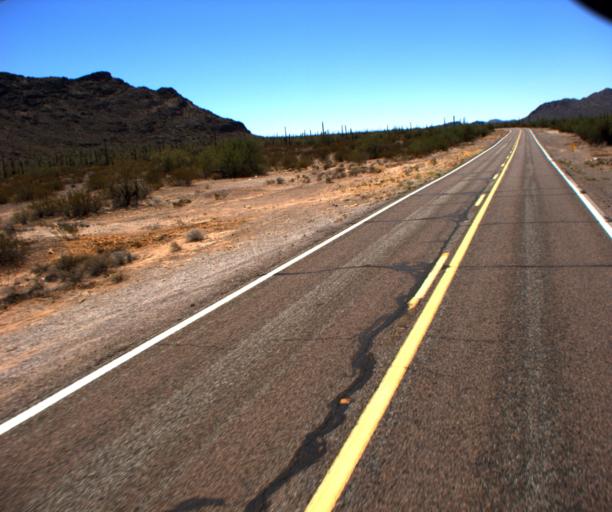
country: US
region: Arizona
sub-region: Pima County
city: Ajo
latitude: 32.2308
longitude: -112.7126
